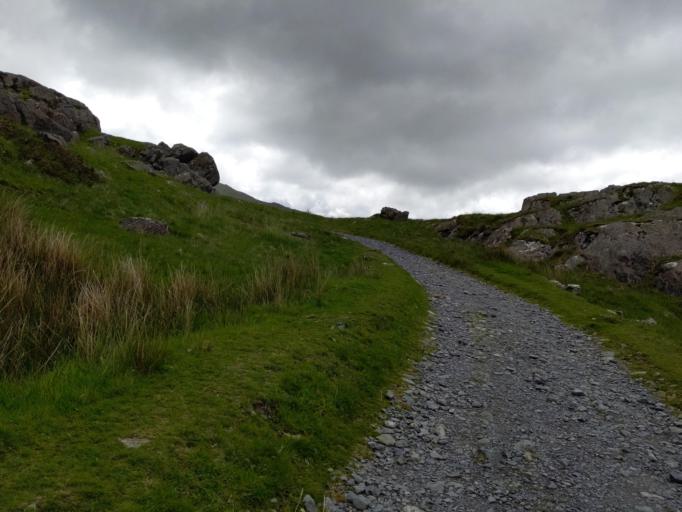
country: GB
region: Wales
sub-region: Gwynedd
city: Llanberis
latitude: 53.0508
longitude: -4.1170
